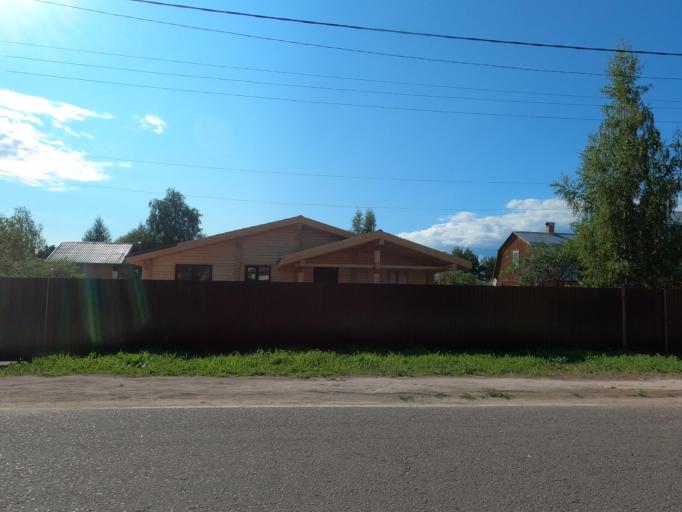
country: RU
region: Moskovskaya
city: Lopatinskiy
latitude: 55.3943
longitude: 38.7168
